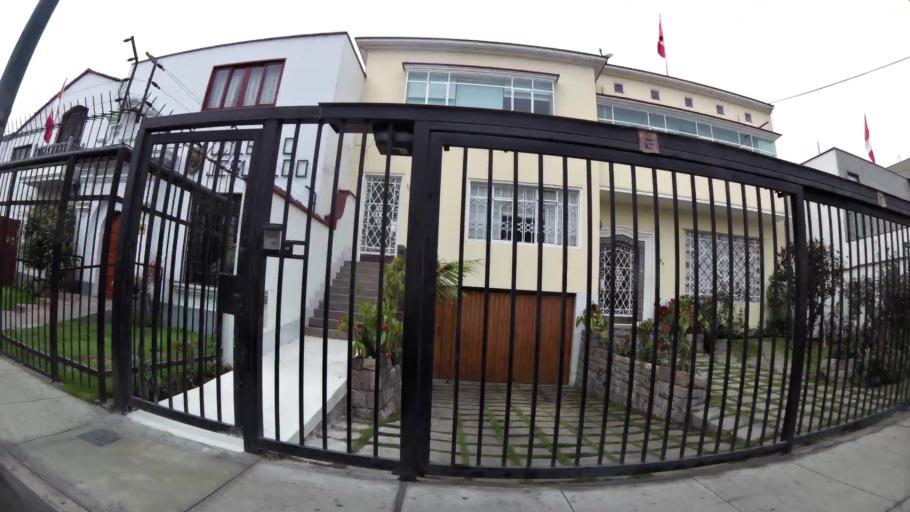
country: PE
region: Lima
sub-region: Lima
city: San Isidro
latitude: -12.0891
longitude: -77.0480
